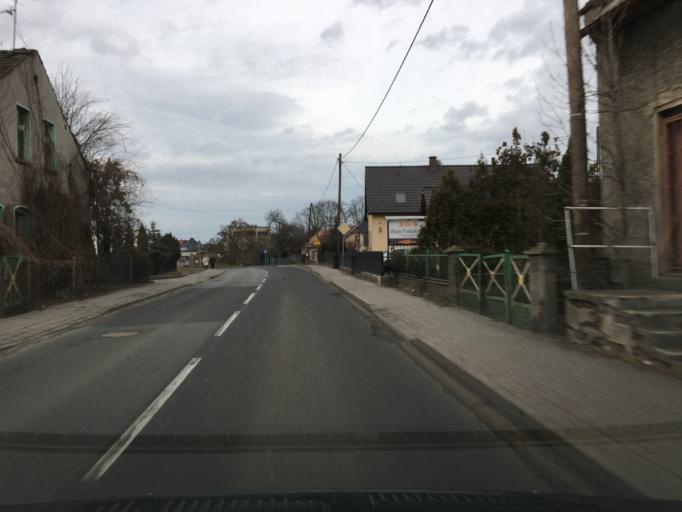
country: PL
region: Opole Voivodeship
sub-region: Powiat kedzierzynsko-kozielski
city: Kozle
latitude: 50.3509
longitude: 18.1669
